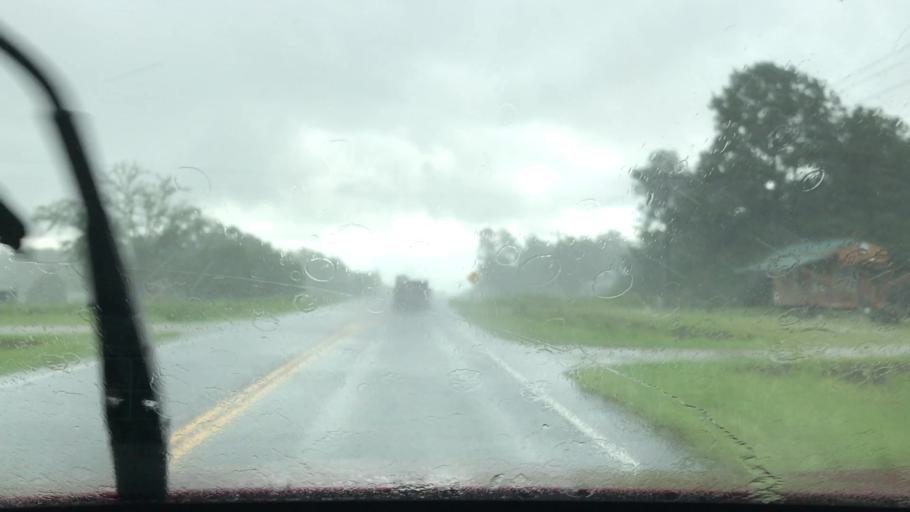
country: US
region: South Carolina
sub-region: Horry County
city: Loris
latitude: 33.9021
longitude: -78.8691
